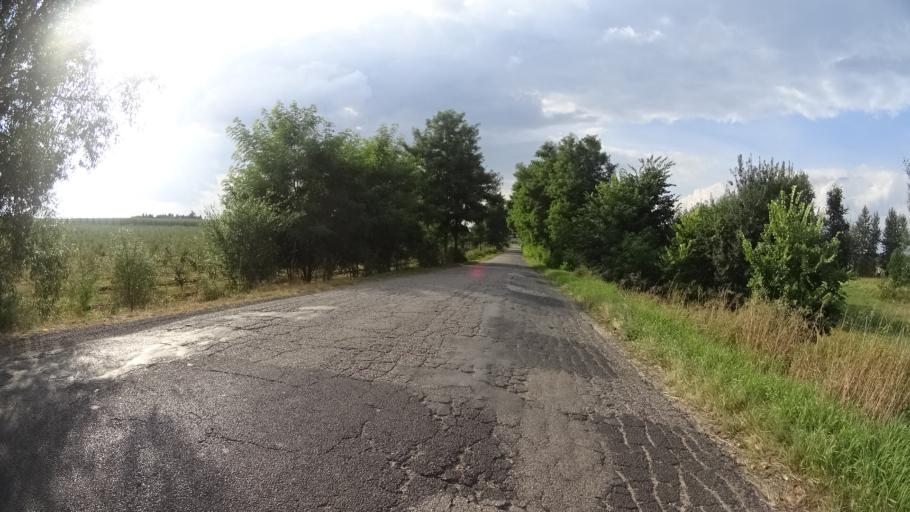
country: PL
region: Masovian Voivodeship
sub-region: Powiat grojecki
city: Mogielnica
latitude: 51.6664
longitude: 20.7415
